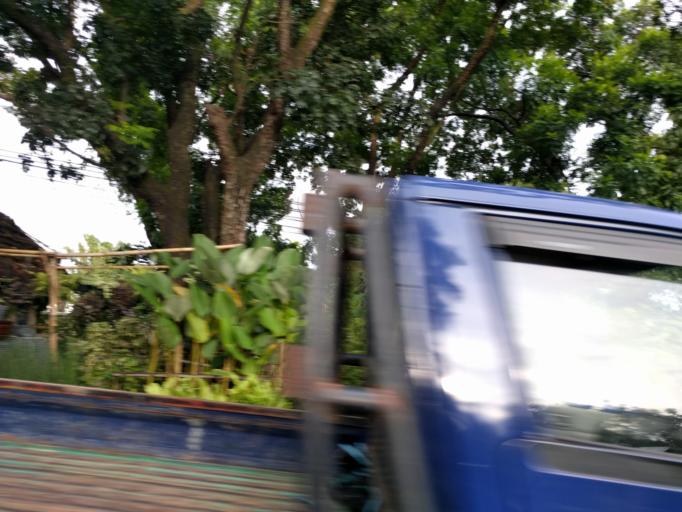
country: ID
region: West Java
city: Bogor
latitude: -6.5843
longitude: 106.8062
